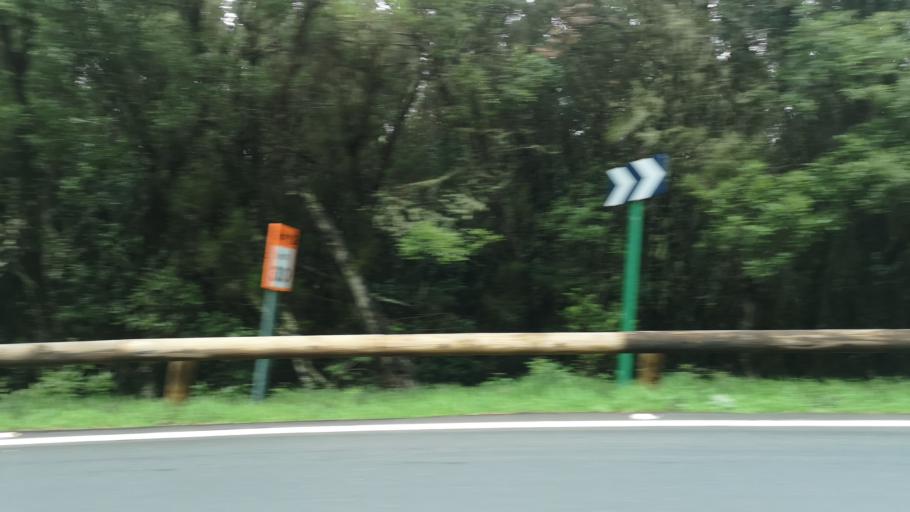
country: ES
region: Canary Islands
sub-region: Provincia de Santa Cruz de Tenerife
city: Vallehermosa
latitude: 28.1350
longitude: -17.2795
